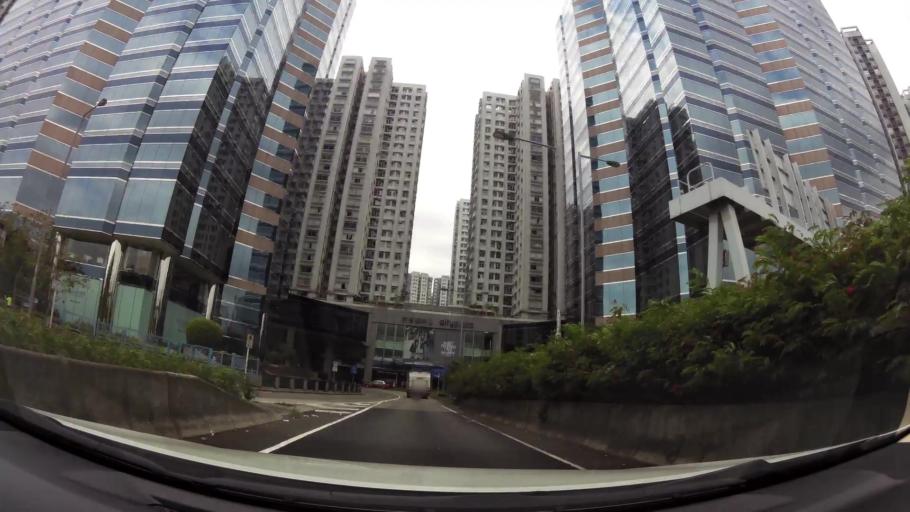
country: HK
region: Kowloon City
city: Kowloon
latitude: 22.2880
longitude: 114.2173
